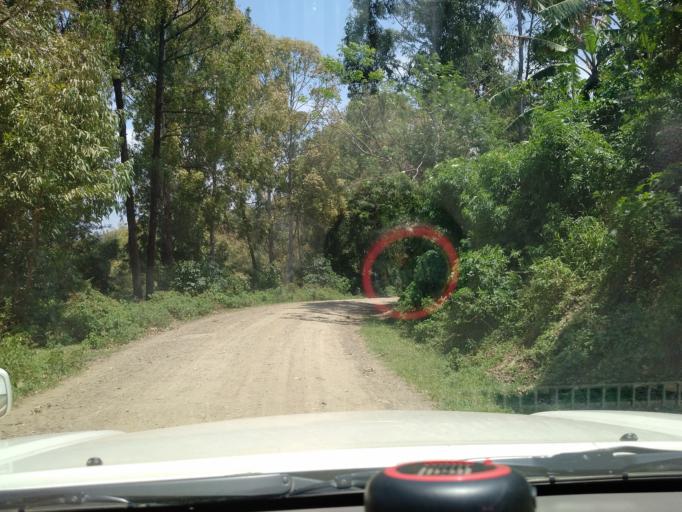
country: CD
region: Nord Kivu
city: Sake
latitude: -1.7788
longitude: 29.0115
